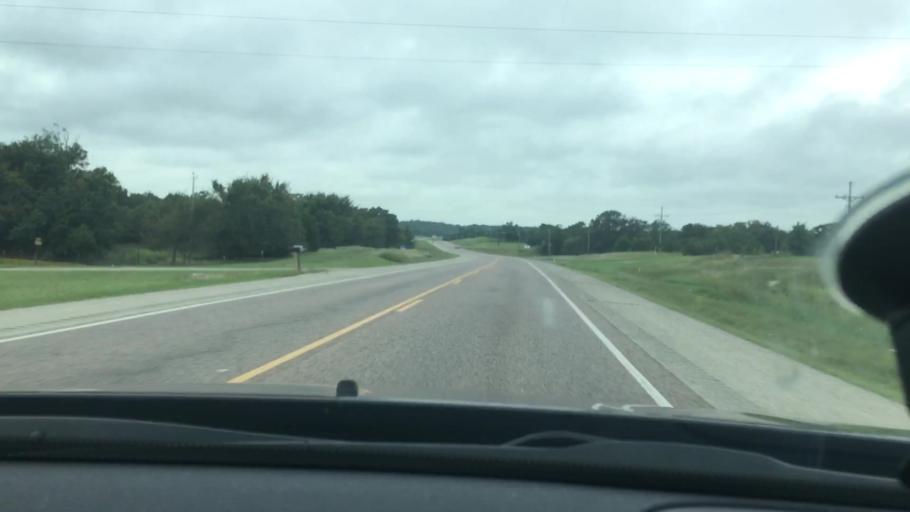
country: US
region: Oklahoma
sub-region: Pontotoc County
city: Ada
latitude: 34.7968
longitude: -96.5509
